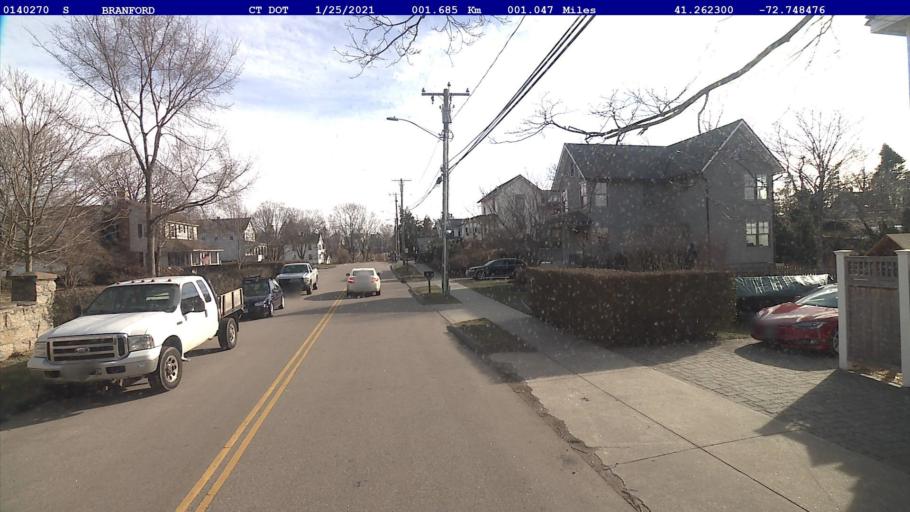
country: US
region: Connecticut
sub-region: New Haven County
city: North Branford
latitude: 41.2623
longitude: -72.7485
